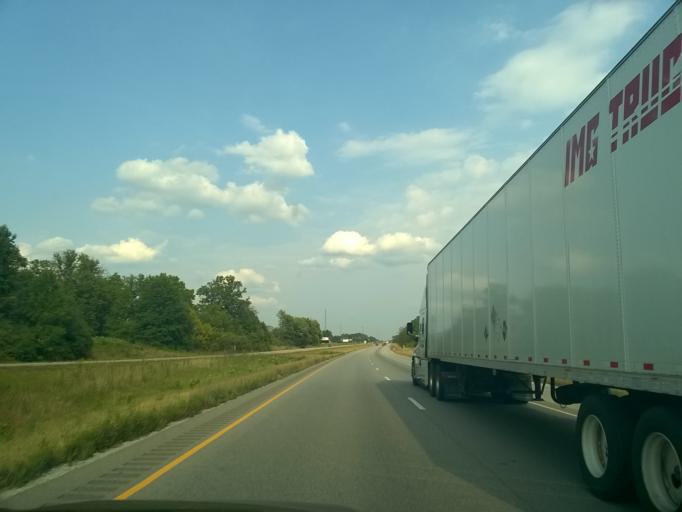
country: US
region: Indiana
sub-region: Vigo County
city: Seelyville
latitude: 39.4457
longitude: -87.2487
